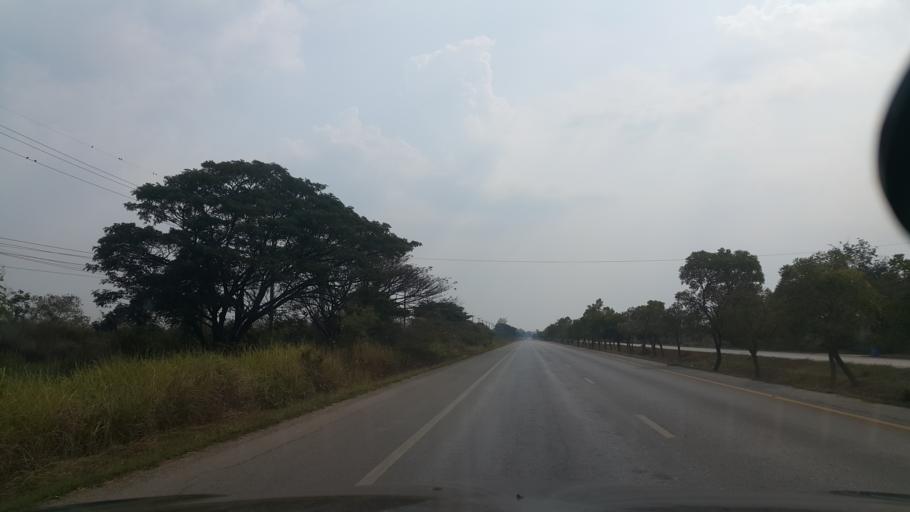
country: TH
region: Sukhothai
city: Sukhothai
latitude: 17.0623
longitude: 99.8841
